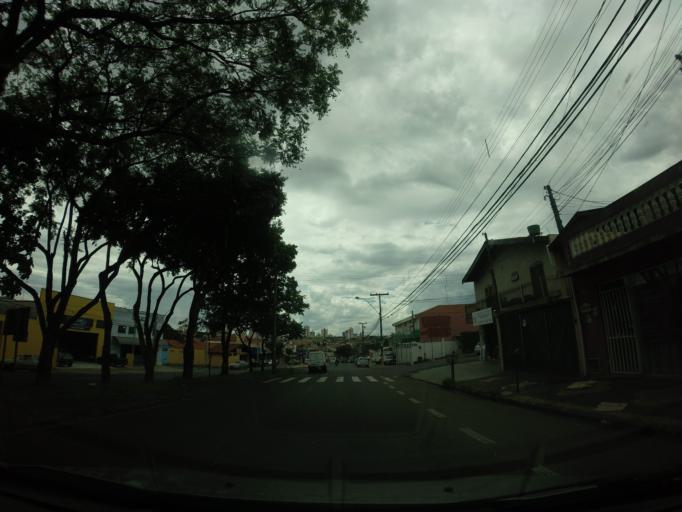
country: BR
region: Sao Paulo
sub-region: Piracicaba
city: Piracicaba
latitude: -22.7425
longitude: -47.6255
